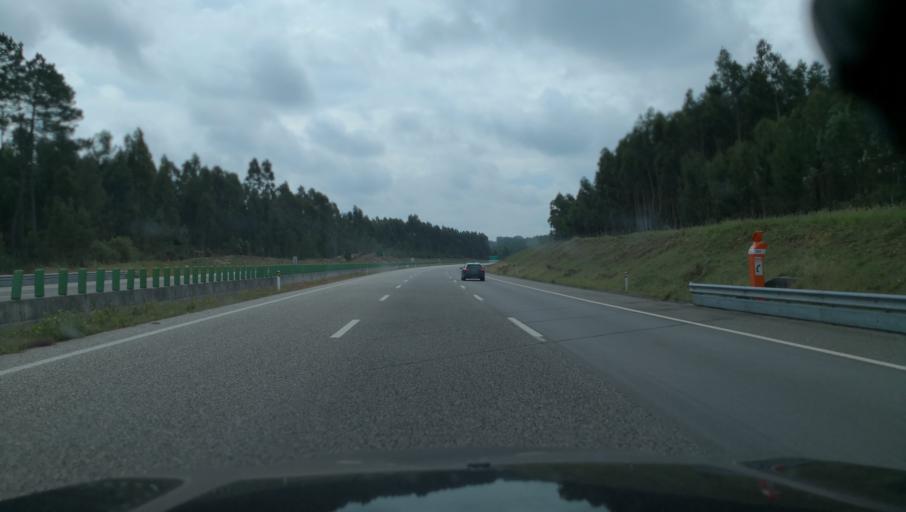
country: PT
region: Leiria
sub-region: Pombal
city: Lourical
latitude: 39.9851
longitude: -8.7902
